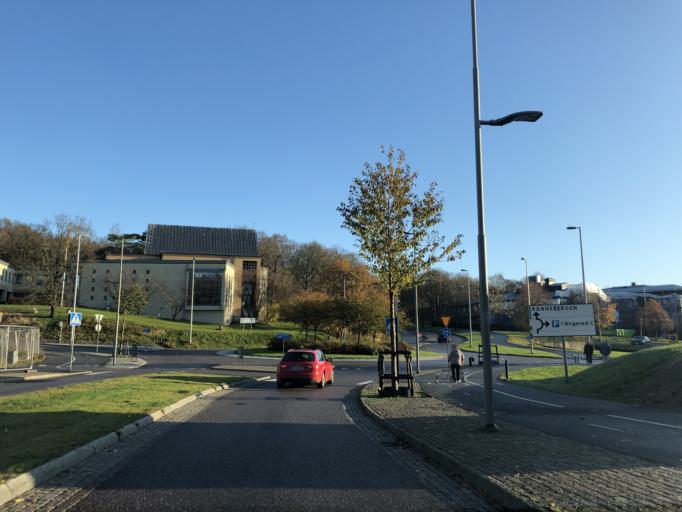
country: SE
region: Vaestra Goetaland
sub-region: Goteborg
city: Loevgaerdet
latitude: 57.7981
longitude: 12.0487
